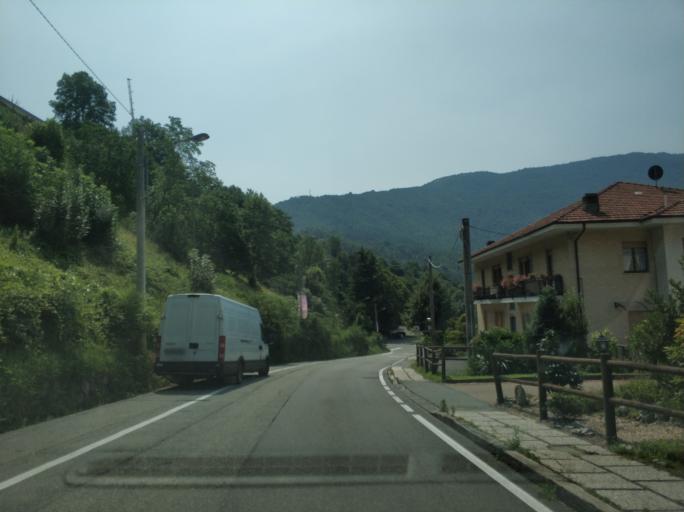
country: IT
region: Piedmont
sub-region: Provincia di Torino
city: Lanzo Torinese
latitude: 45.2716
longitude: 7.4765
